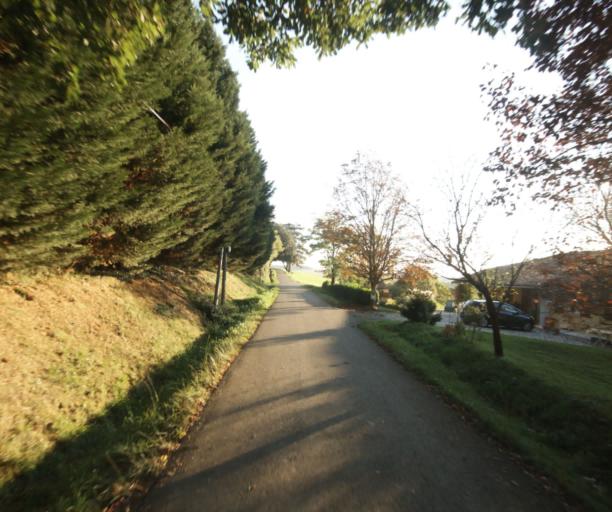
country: FR
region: Midi-Pyrenees
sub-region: Departement du Gers
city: Eauze
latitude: 43.7616
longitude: 0.1652
